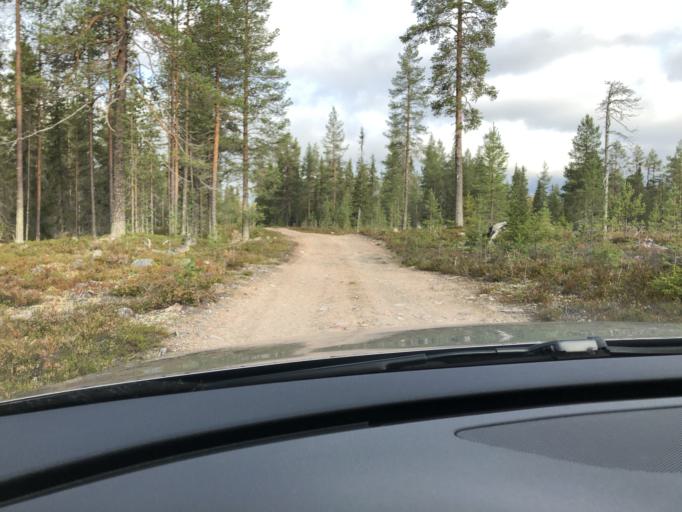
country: FI
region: Lapland
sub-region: Itae-Lappi
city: Posio
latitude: 66.0607
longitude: 27.8119
